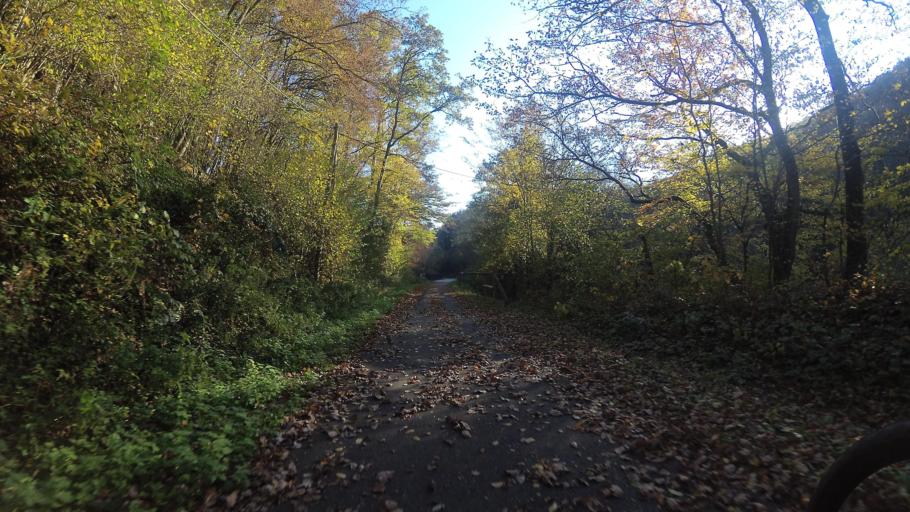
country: DE
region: Rheinland-Pfalz
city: Gutweiler
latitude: 49.7135
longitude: 6.7359
